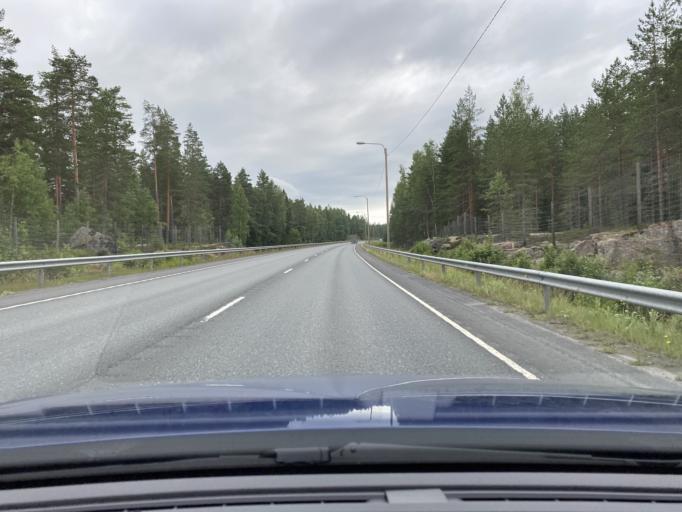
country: FI
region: Pirkanmaa
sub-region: Tampere
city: Kangasala
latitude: 61.5862
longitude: 24.1229
